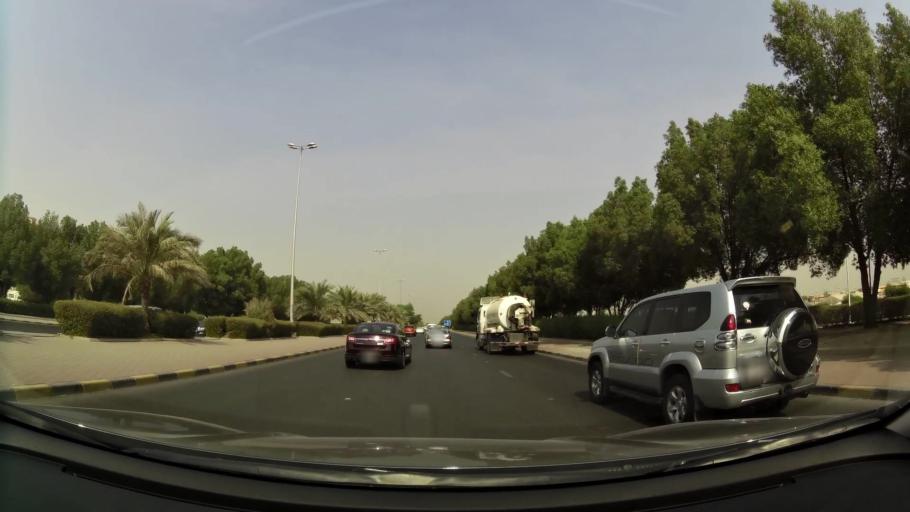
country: KW
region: Al Asimah
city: Ar Rabiyah
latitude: 29.2806
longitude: 47.9069
